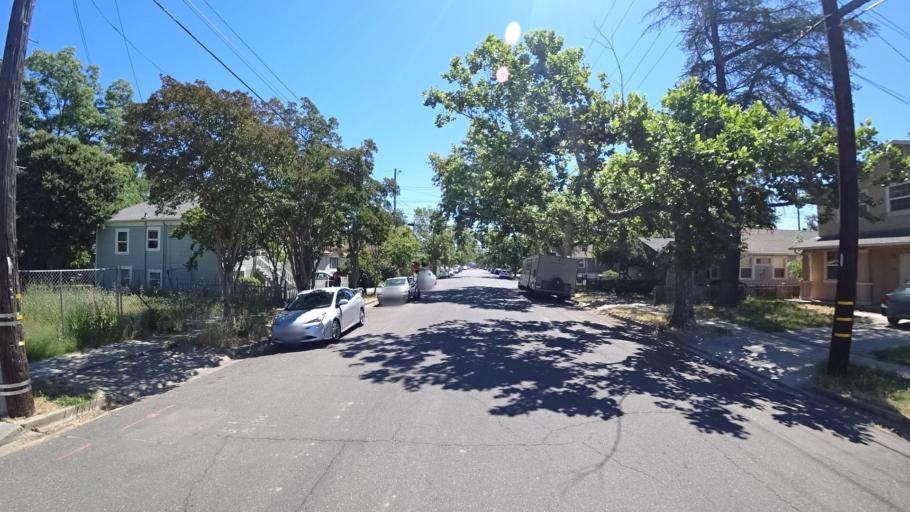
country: US
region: California
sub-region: Sacramento County
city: Sacramento
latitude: 38.5483
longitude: -121.4583
